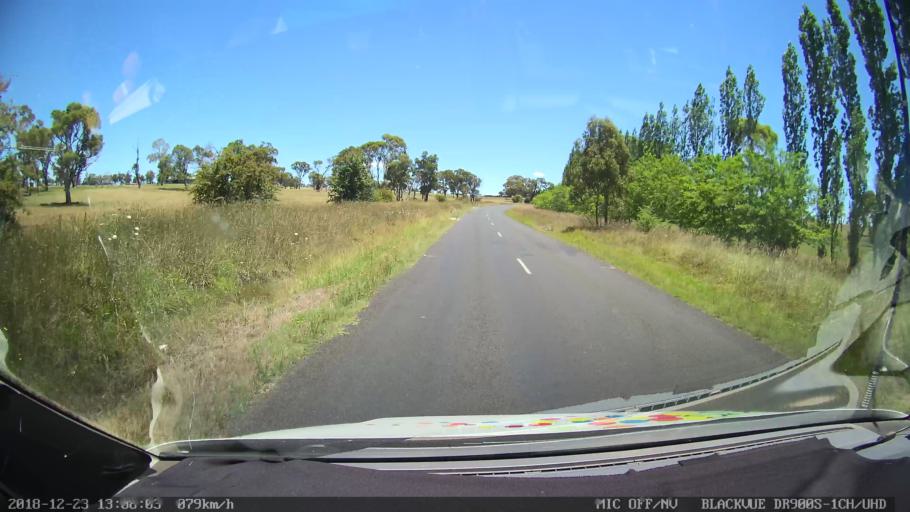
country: AU
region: New South Wales
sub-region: Armidale Dumaresq
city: Armidale
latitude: -30.5147
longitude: 151.6221
